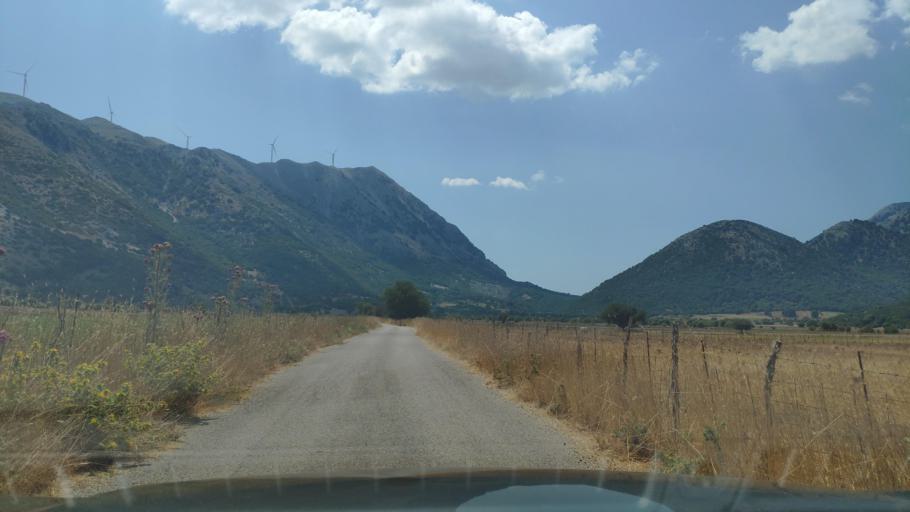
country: GR
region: West Greece
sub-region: Nomos Aitolias kai Akarnanias
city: Monastirakion
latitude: 38.7867
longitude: 20.9659
